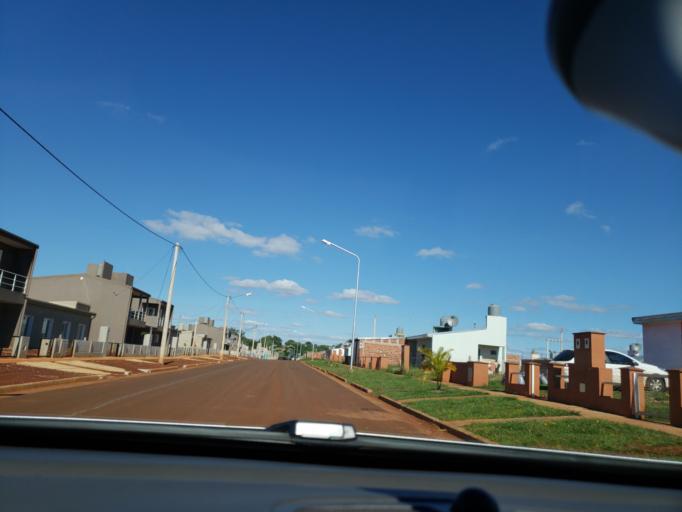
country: AR
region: Misiones
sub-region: Departamento de Capital
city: Posadas
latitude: -27.4038
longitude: -55.9843
